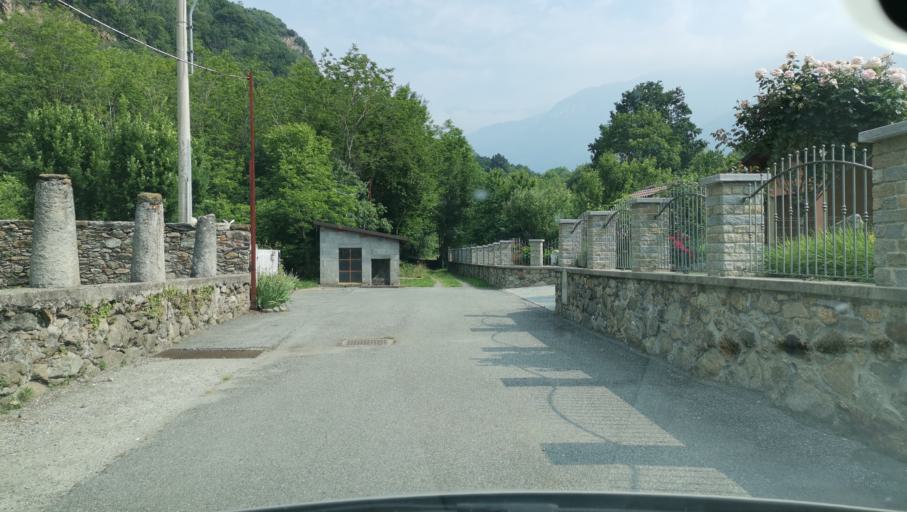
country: IT
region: Piedmont
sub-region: Provincia di Torino
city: Quassolo
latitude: 45.5262
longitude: 7.8308
